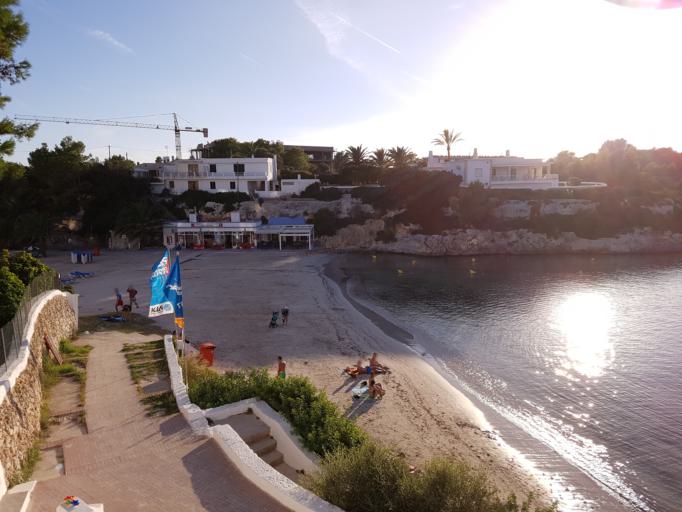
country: ES
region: Balearic Islands
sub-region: Illes Balears
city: Ciutadella
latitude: 39.9782
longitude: 3.8397
